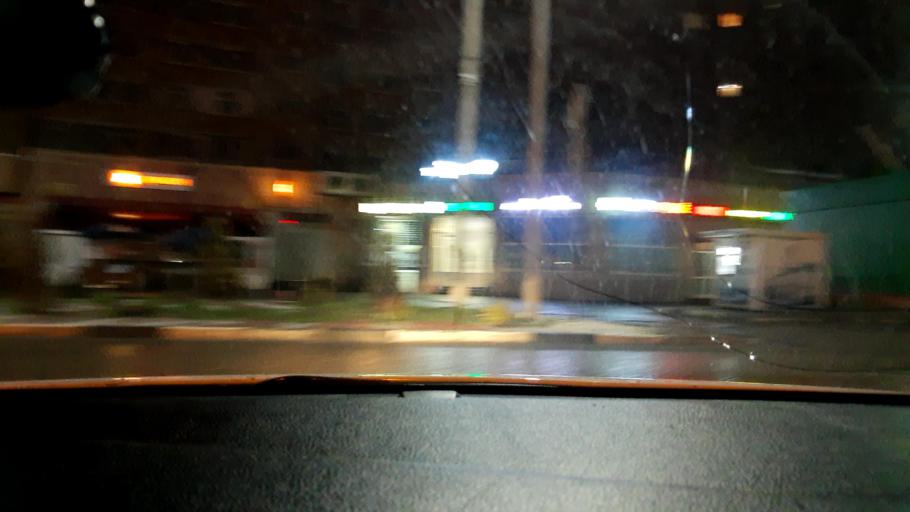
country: RU
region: Moskovskaya
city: Nakhabino
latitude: 55.8471
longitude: 37.1767
